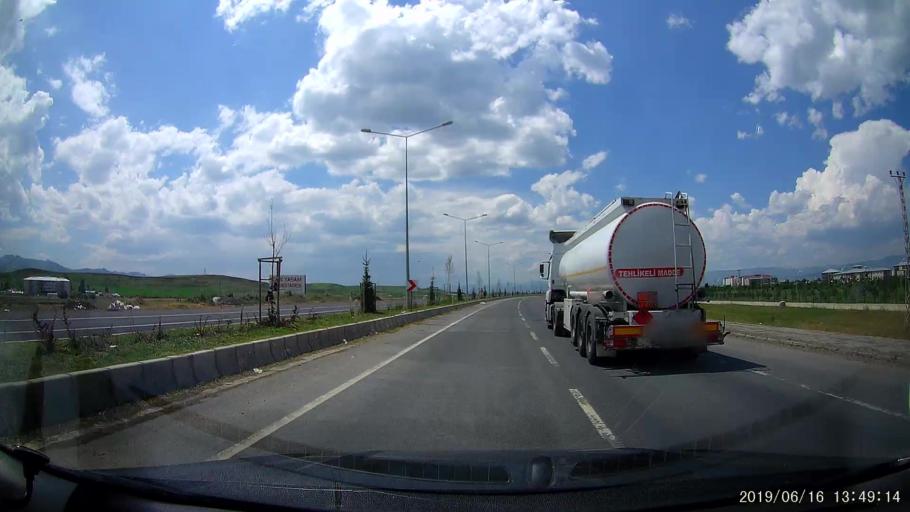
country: TR
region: Agri
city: Agri
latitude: 39.7158
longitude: 42.9938
